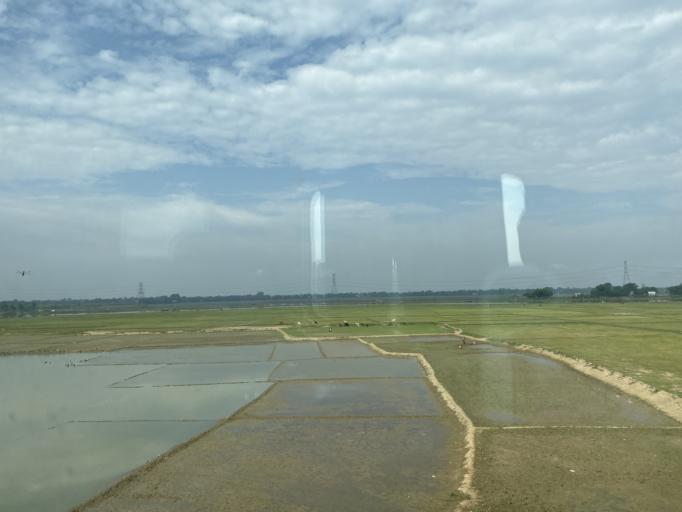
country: IN
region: Tripura
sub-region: West Tripura
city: Agartala
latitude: 23.8821
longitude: 91.2051
